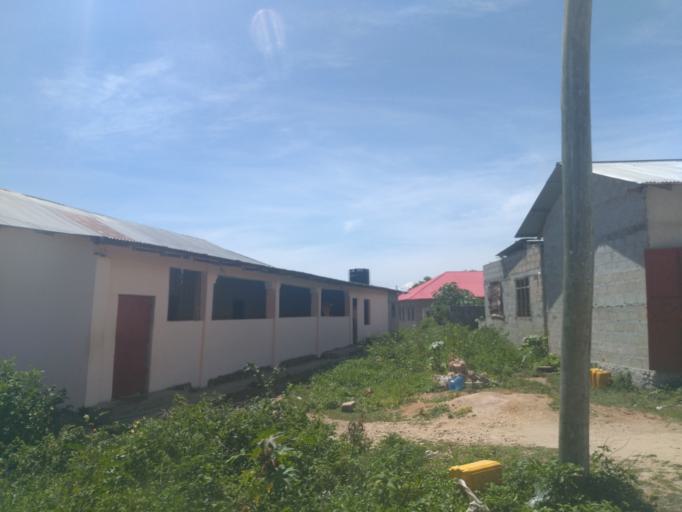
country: TZ
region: Zanzibar North
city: Gamba
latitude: -5.9248
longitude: 39.3551
